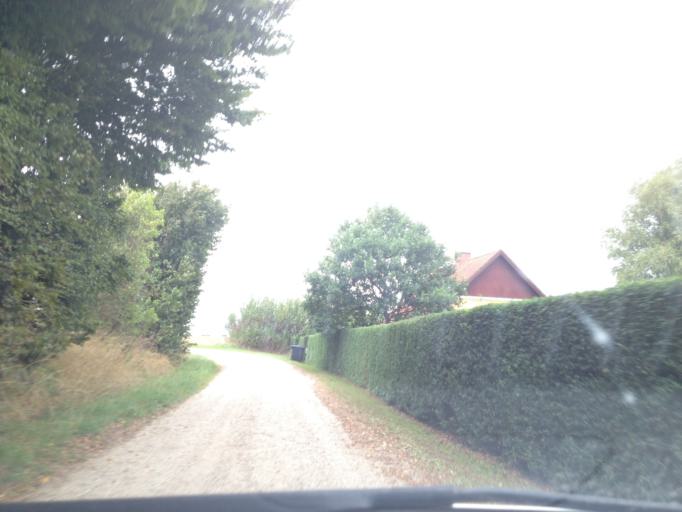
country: DK
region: South Denmark
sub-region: Haderslev Kommune
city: Starup
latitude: 55.3009
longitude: 9.5539
